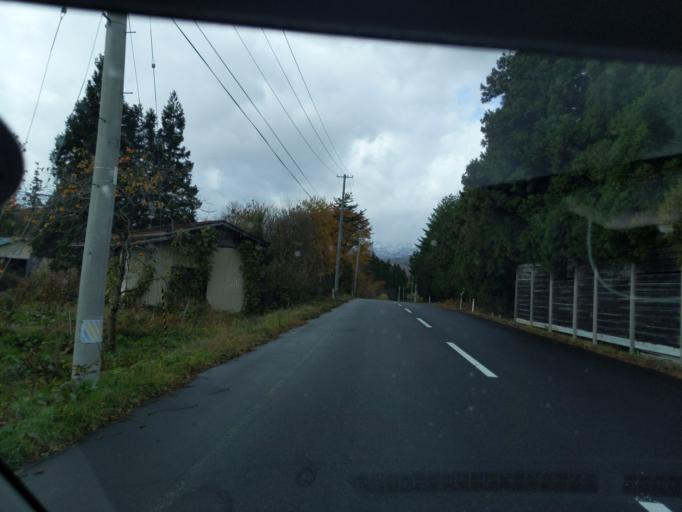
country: JP
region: Iwate
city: Mizusawa
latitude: 39.1116
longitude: 140.9618
